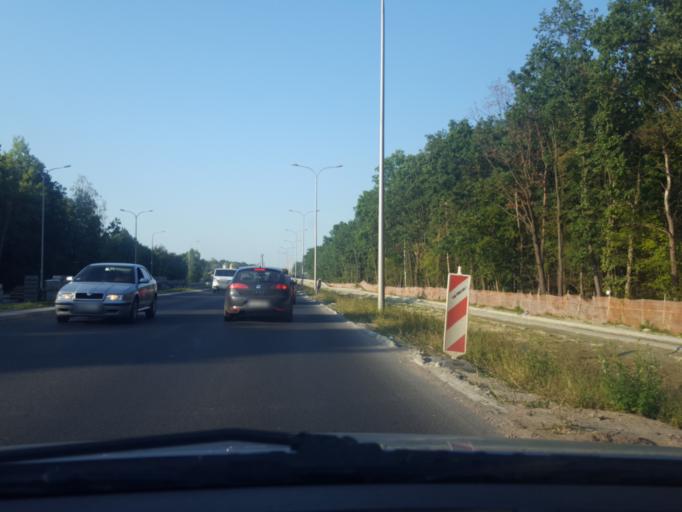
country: PL
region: Masovian Voivodeship
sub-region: Warszawa
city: Rembertow
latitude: 52.2531
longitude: 21.1401
